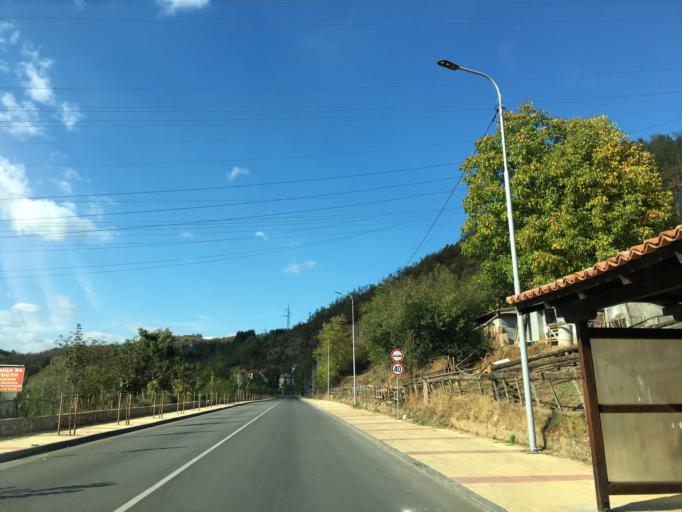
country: BG
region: Smolyan
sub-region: Obshtina Zlatograd
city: Zlatograd
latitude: 41.3883
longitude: 25.0876
